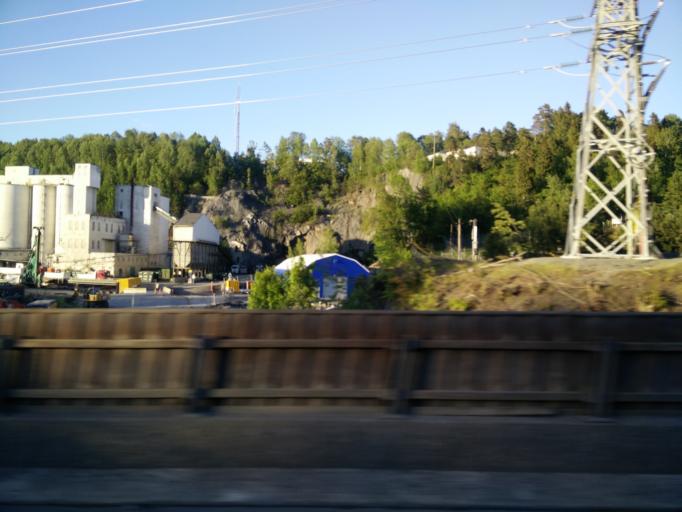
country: NO
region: Akershus
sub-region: Asker
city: Billingstad
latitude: 59.8989
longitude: 10.4968
